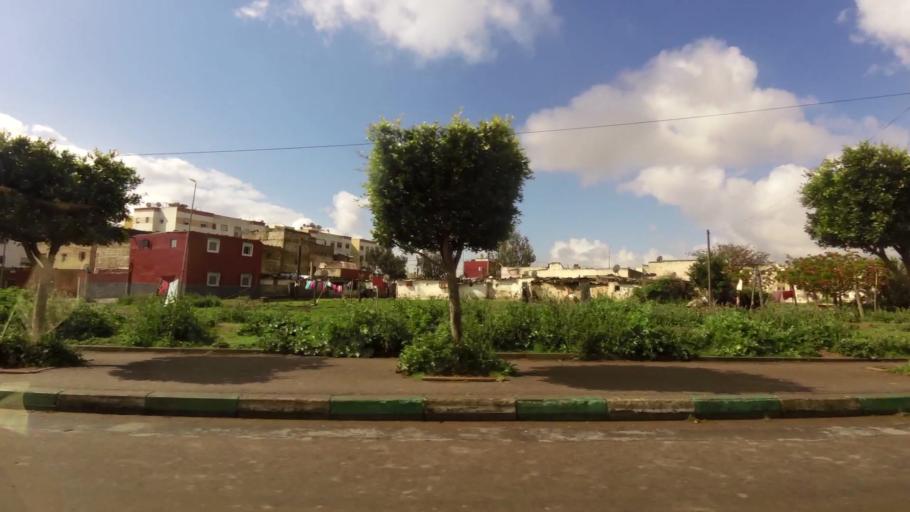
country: MA
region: Grand Casablanca
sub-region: Nouaceur
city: Bouskoura
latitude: 33.5327
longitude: -7.6809
